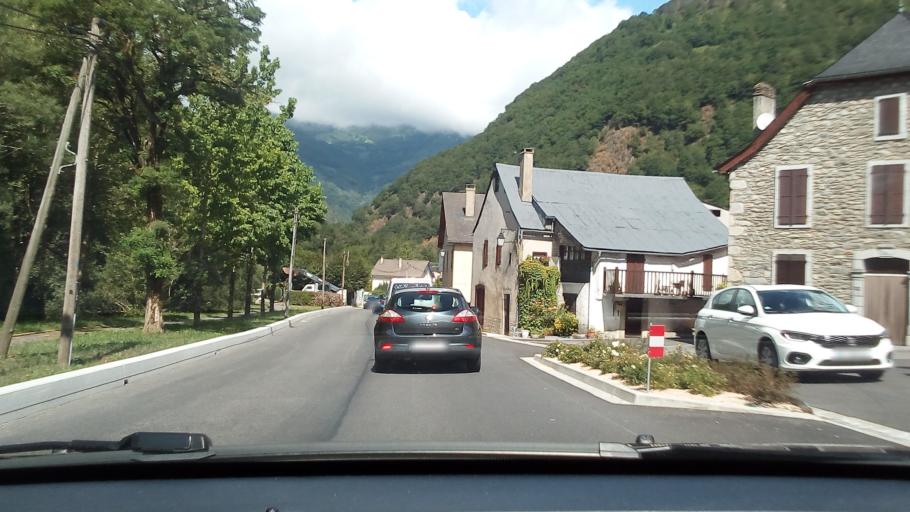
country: FR
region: Aquitaine
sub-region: Departement des Pyrenees-Atlantiques
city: Laruns
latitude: 42.9354
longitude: -0.5880
